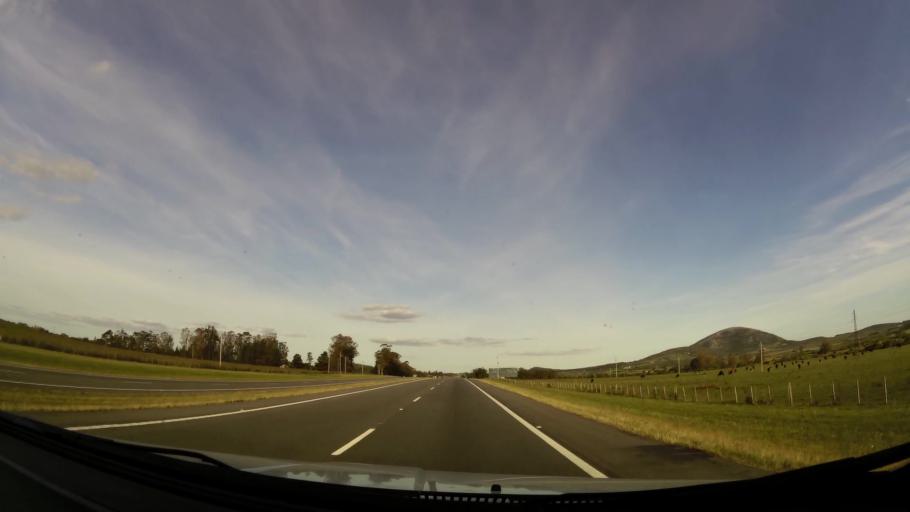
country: UY
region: Maldonado
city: Pan de Azucar
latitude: -34.7906
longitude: -55.3075
